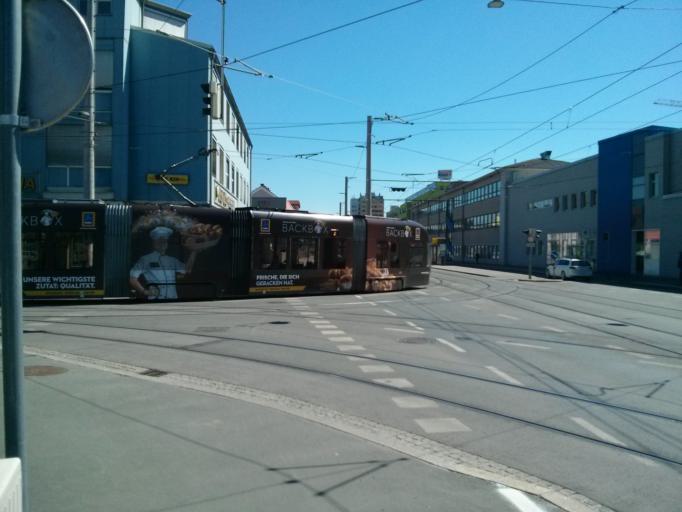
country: AT
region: Styria
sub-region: Graz Stadt
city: Wetzelsdorf
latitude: 47.0706
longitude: 15.4129
